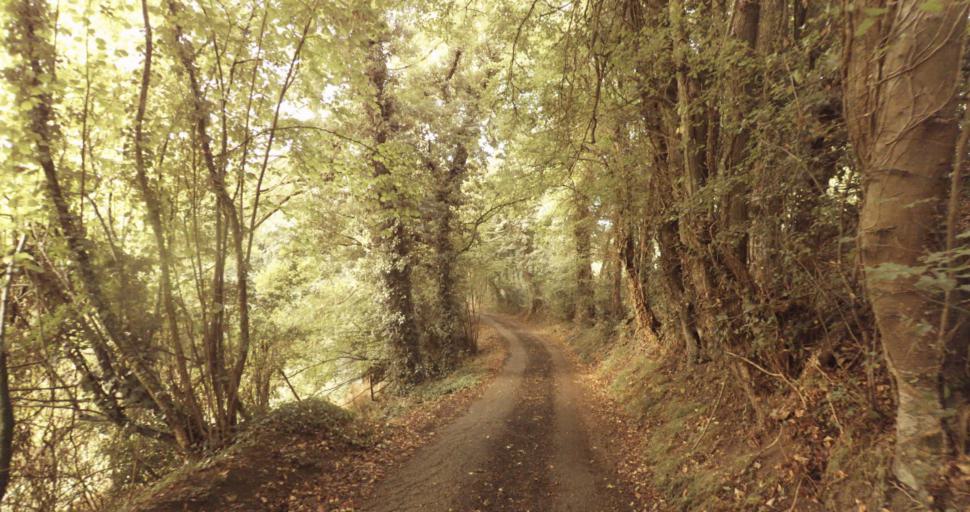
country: FR
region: Lower Normandy
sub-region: Departement de l'Orne
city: Vimoutiers
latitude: 48.9185
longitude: 0.2208
